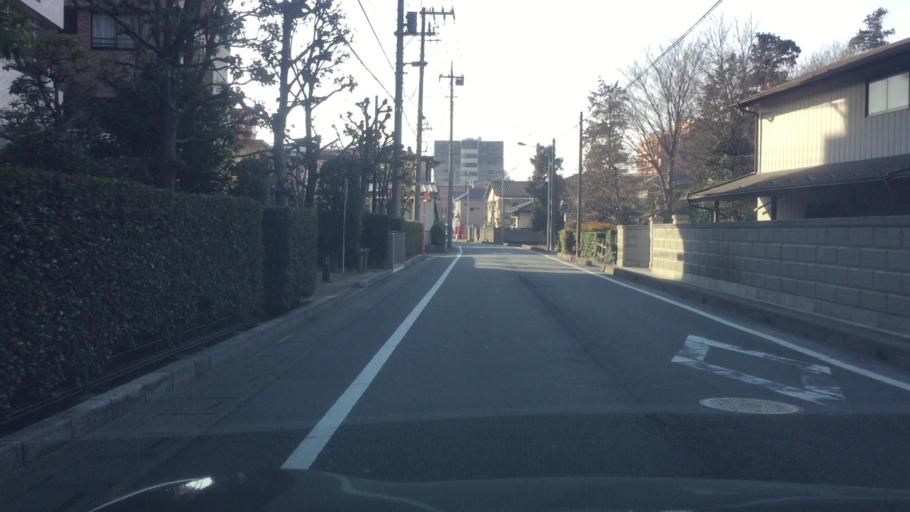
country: JP
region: Saitama
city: Ageoshimo
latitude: 35.9290
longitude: 139.6141
